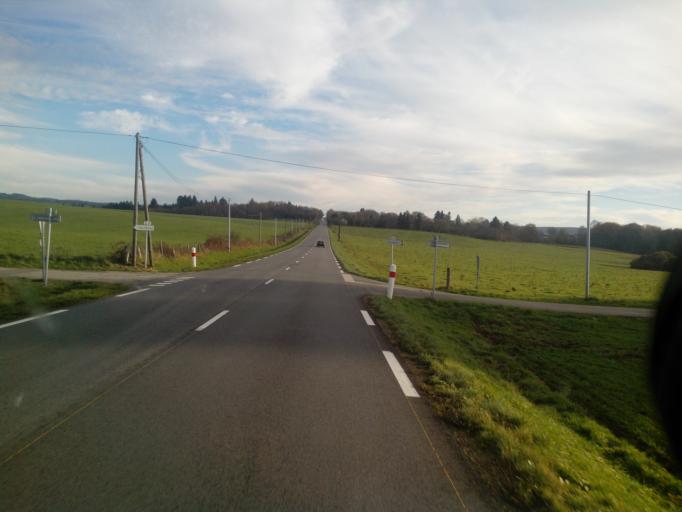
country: FR
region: Limousin
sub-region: Departement de la Haute-Vienne
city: Neuvic-Entier
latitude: 45.7499
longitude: 1.5984
